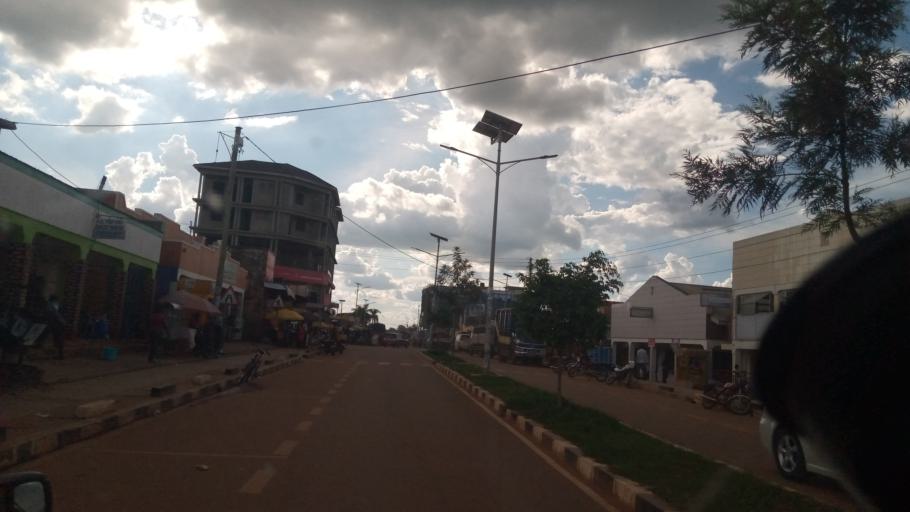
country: UG
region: Northern Region
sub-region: Lira District
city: Lira
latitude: 2.2420
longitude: 32.8982
